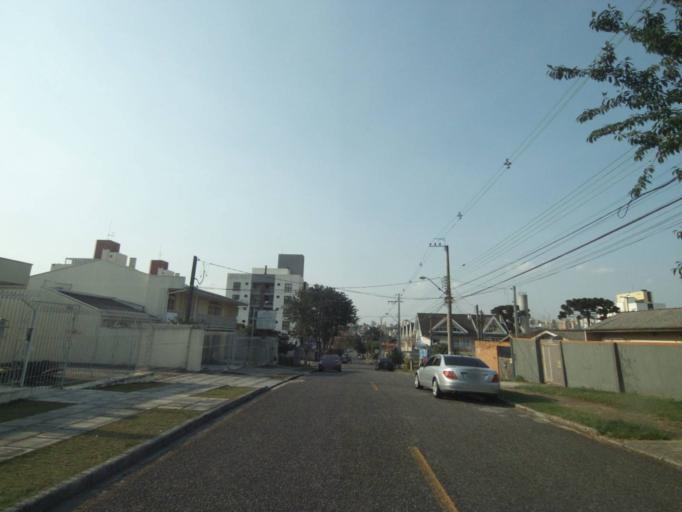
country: BR
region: Parana
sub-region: Curitiba
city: Curitiba
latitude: -25.4620
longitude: -49.3004
